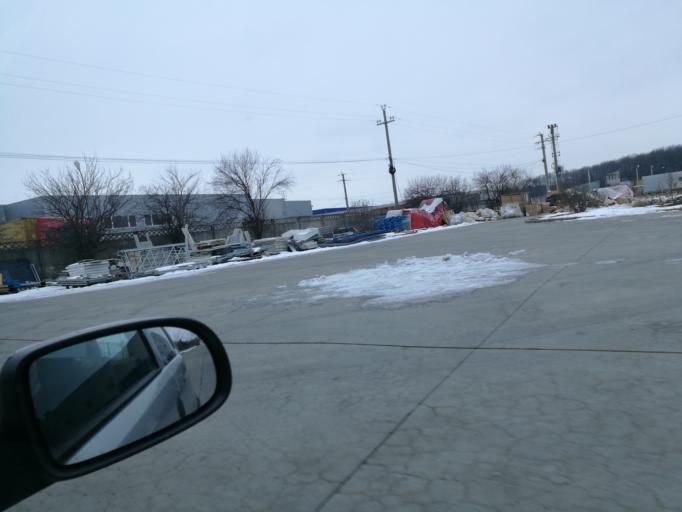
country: RO
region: Ilfov
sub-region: Comuna Tunari
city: Tunari
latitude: 44.5397
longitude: 26.1321
